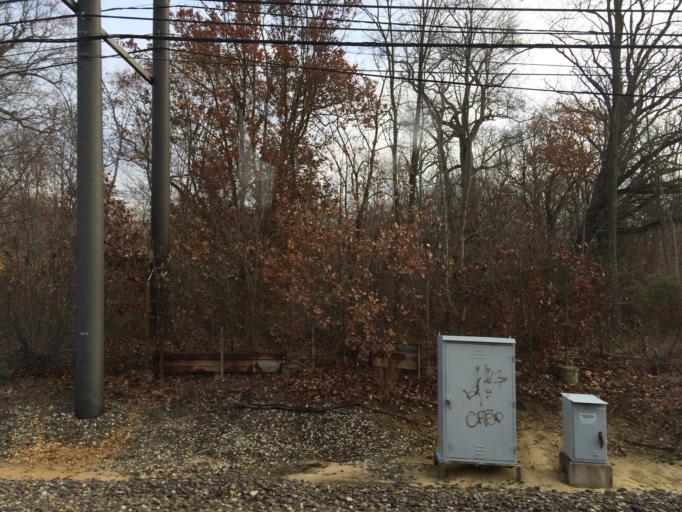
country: US
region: New Jersey
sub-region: Camden County
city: Ashland
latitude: 39.8681
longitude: -75.0101
